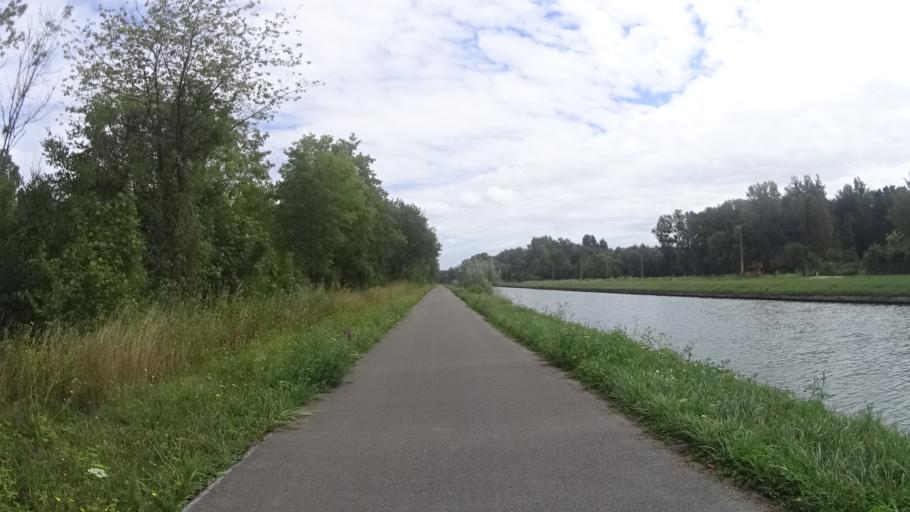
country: FR
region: Picardie
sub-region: Departement de l'Oise
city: Crisolles
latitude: 49.5776
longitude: 3.0845
